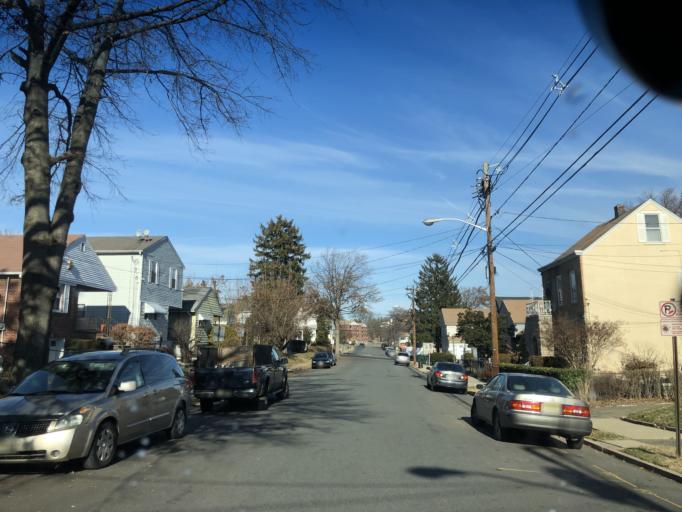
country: US
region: New Jersey
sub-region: Bergen County
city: Fair Lawn
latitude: 40.9271
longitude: -74.1453
